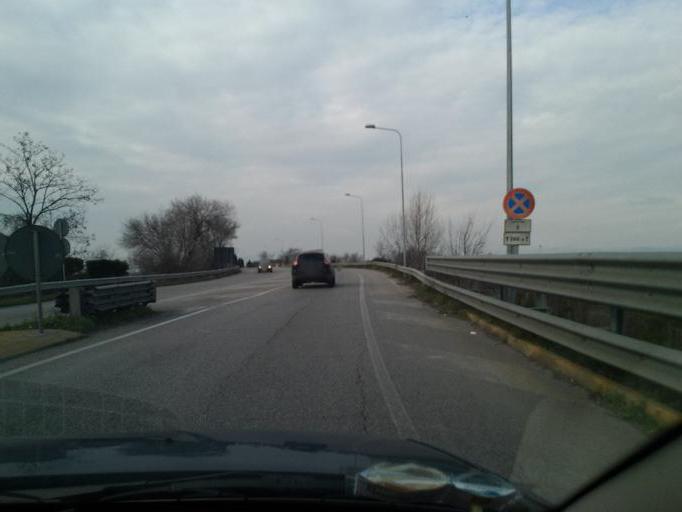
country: IT
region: Veneto
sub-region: Provincia di Verona
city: Sommacampagna
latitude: 45.4149
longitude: 10.8530
